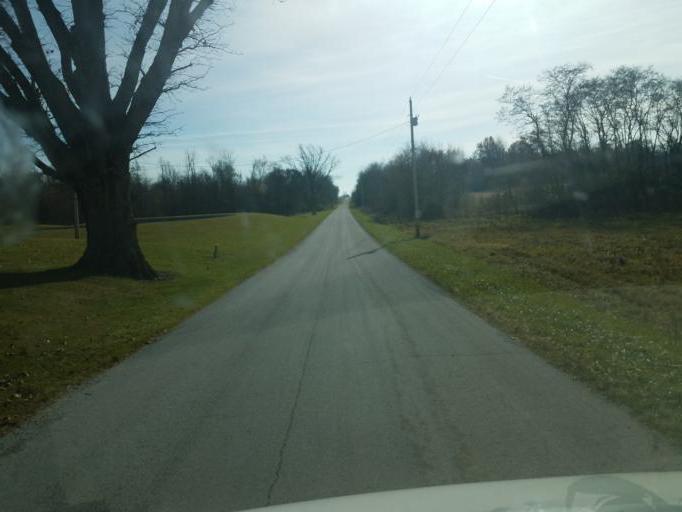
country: US
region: Ohio
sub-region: Hardin County
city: Forest
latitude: 40.6563
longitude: -83.4393
